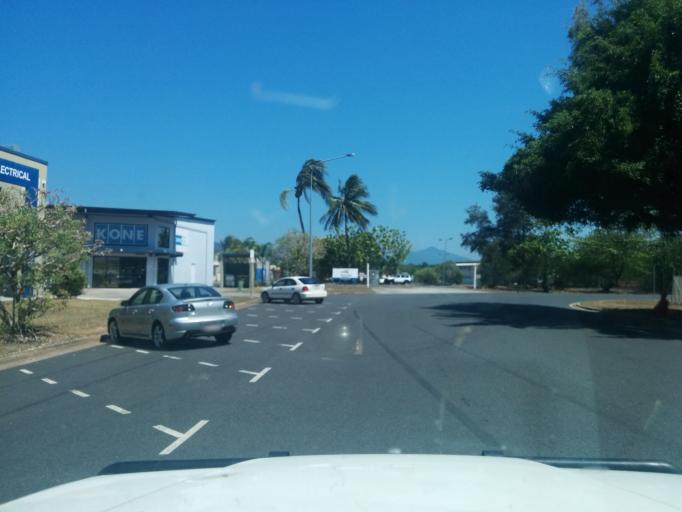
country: AU
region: Queensland
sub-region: Cairns
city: Cairns
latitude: -16.9428
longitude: 145.7730
